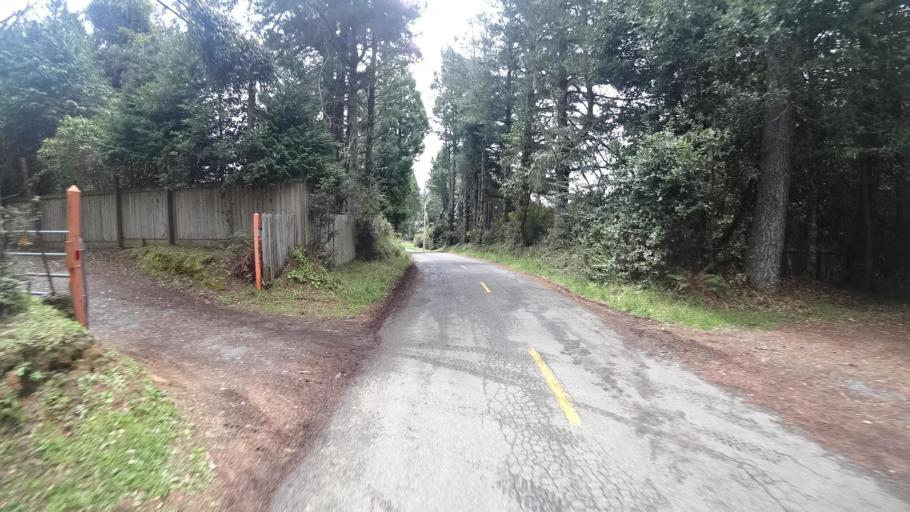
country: US
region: California
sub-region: Humboldt County
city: Bayside
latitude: 40.7695
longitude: -123.9996
